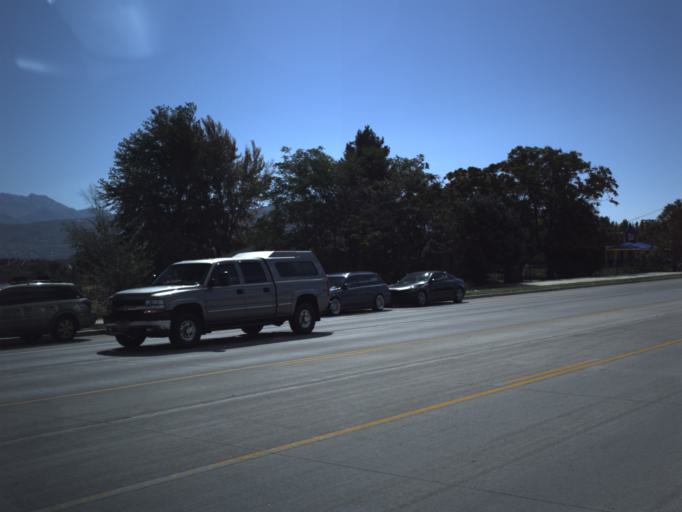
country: US
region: Utah
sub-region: Salt Lake County
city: Riverton
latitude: 40.5415
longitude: -111.9388
